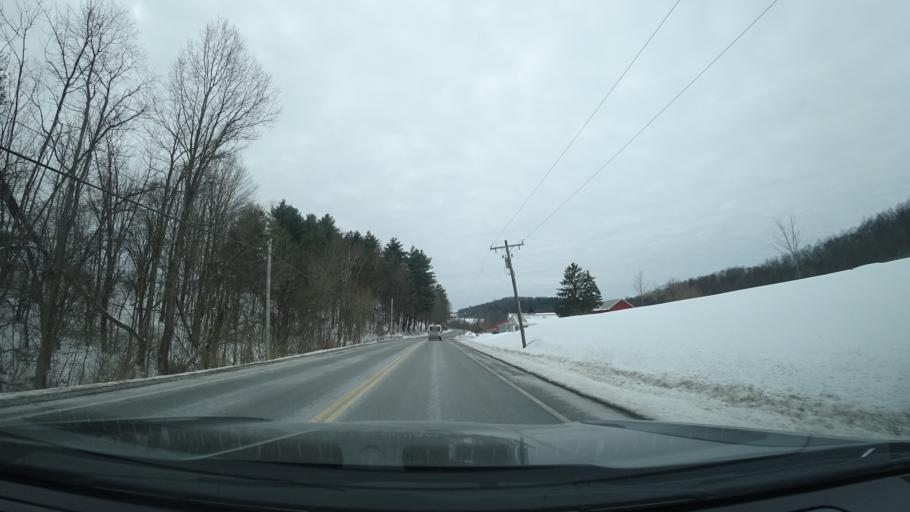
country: US
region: New York
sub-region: Washington County
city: Greenwich
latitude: 43.1905
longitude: -73.4900
